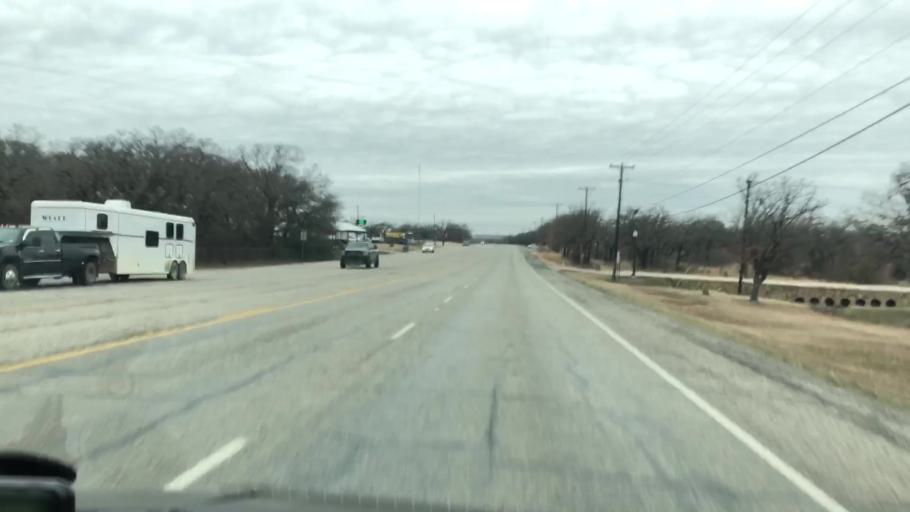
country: US
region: Texas
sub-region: Jack County
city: Jacksboro
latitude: 33.2277
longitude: -98.1717
